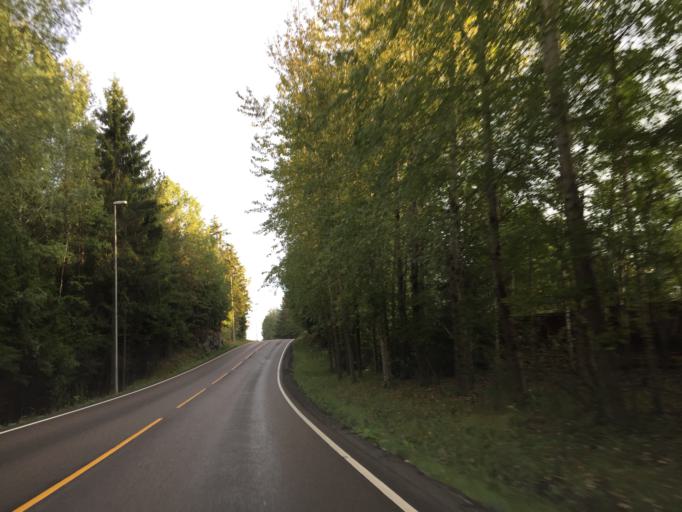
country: NO
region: Akershus
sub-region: Ski
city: Ski
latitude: 59.7707
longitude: 10.8497
